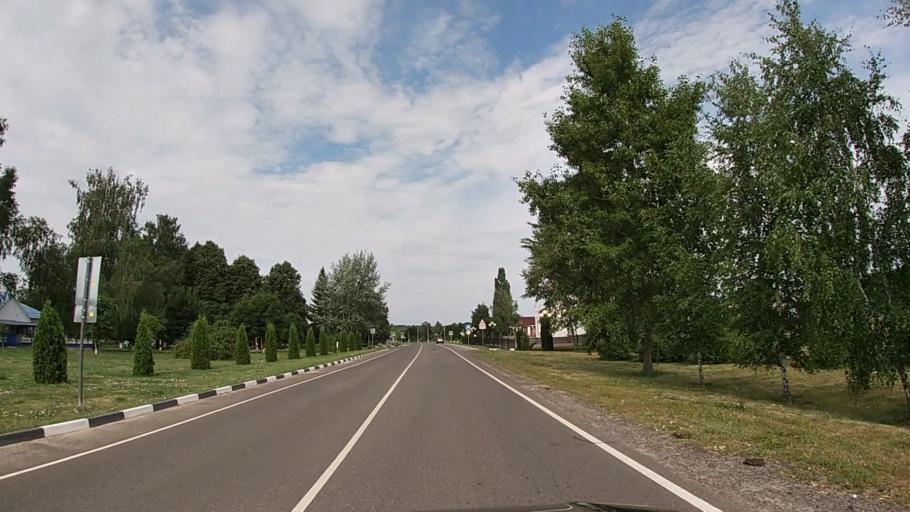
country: UA
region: Sumy
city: Krasnopillya
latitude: 50.8143
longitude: 35.4424
